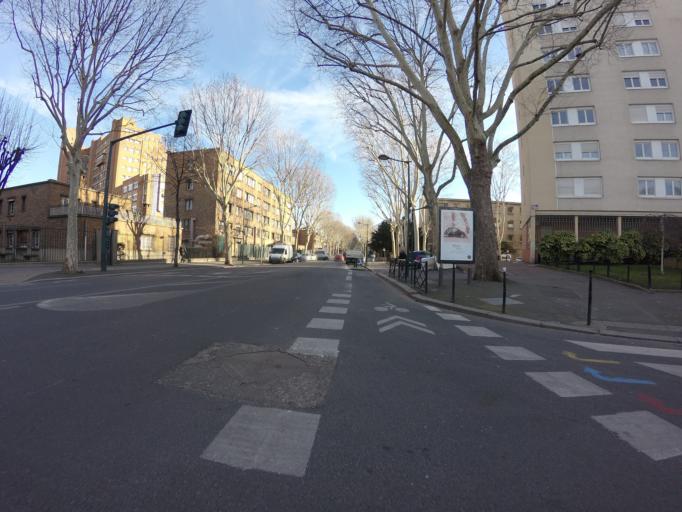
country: FR
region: Ile-de-France
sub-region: Departement des Hauts-de-Seine
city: Clichy
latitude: 48.9081
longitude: 2.3078
